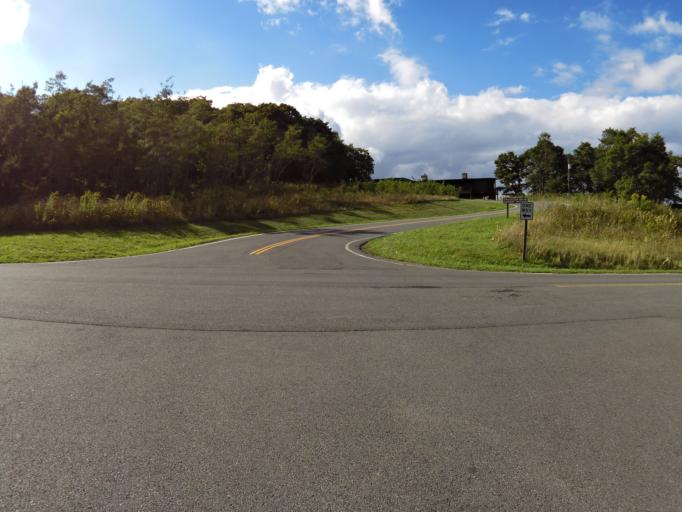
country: US
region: Virginia
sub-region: Page County
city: Luray
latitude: 38.5912
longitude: -78.3836
